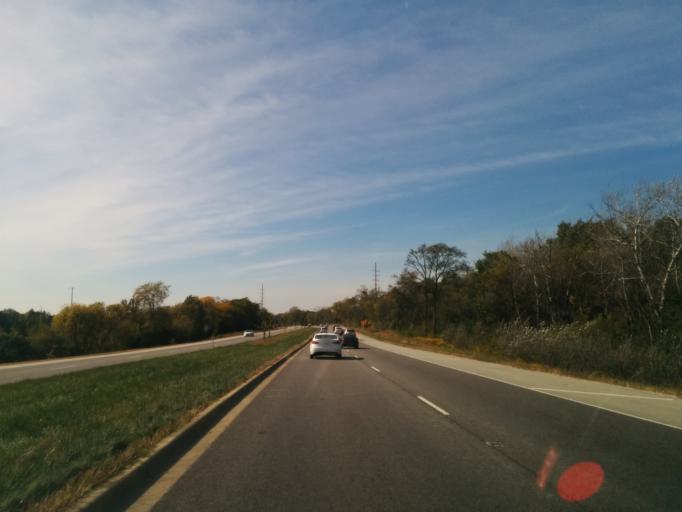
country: US
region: Illinois
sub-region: DuPage County
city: Warrenville
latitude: 41.8303
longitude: -88.1621
